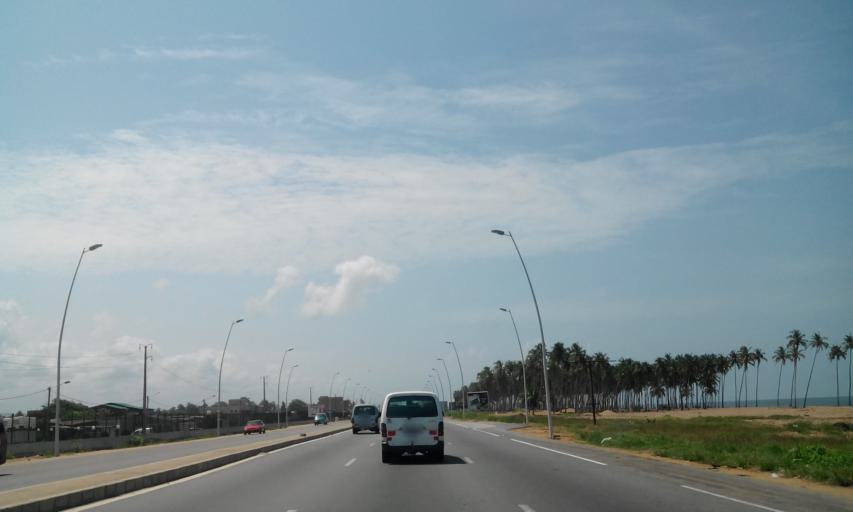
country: CI
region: Lagunes
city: Bingerville
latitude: 5.2384
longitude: -3.8905
